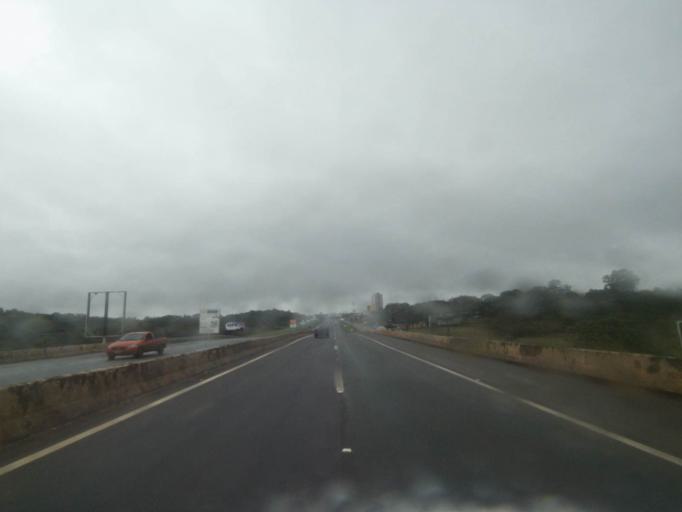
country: PY
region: Alto Parana
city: Ciudad del Este
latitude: -25.5072
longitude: -54.5846
